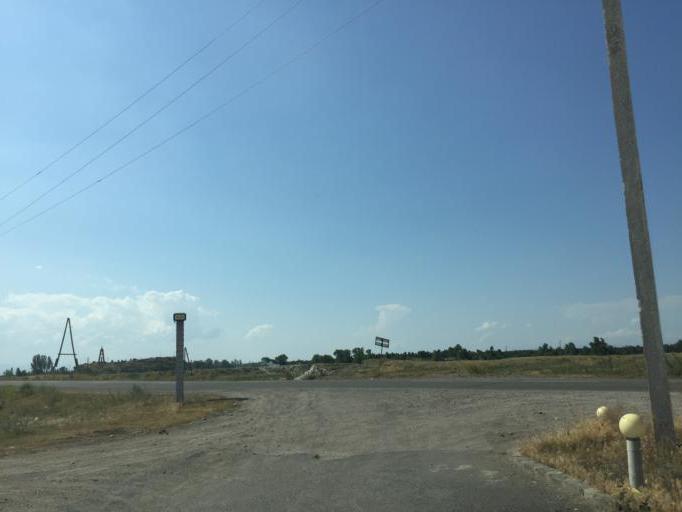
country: AM
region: Geghark'unik'i Marz
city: Tsovinar
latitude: 40.1621
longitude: 45.4782
